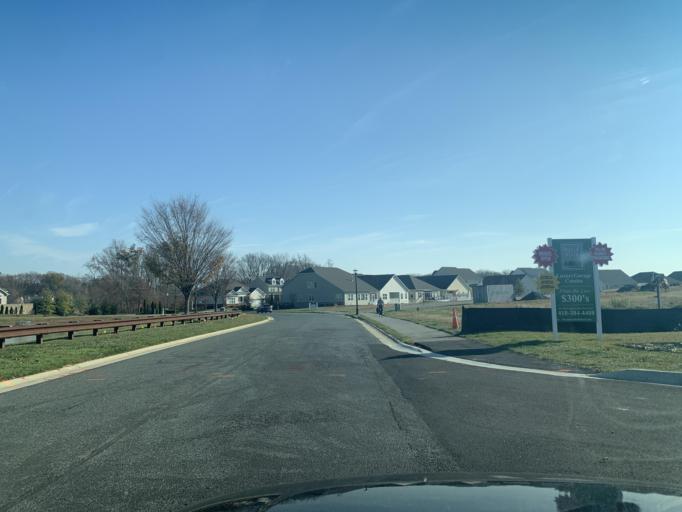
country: US
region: Maryland
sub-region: Harford County
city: Havre de Grace
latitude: 39.5442
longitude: -76.1215
